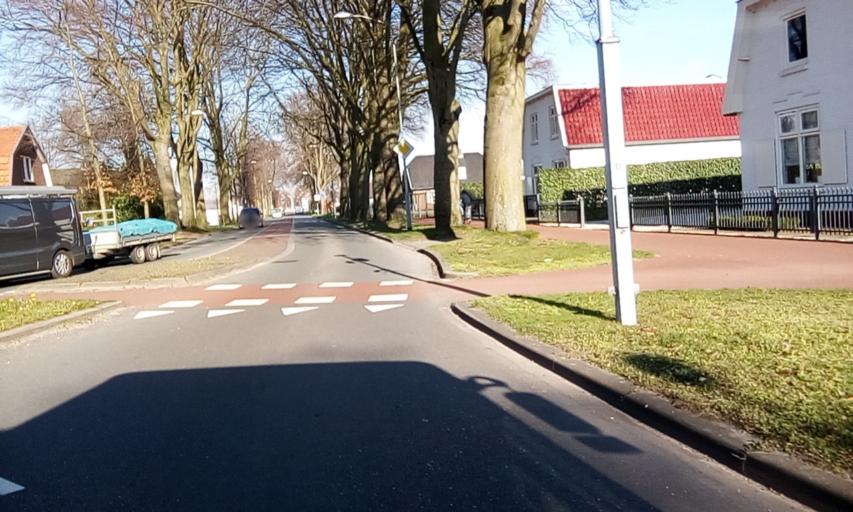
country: NL
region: Gelderland
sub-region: Gemeente Wijchen
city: Wijchen
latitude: 51.8108
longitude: 5.7426
